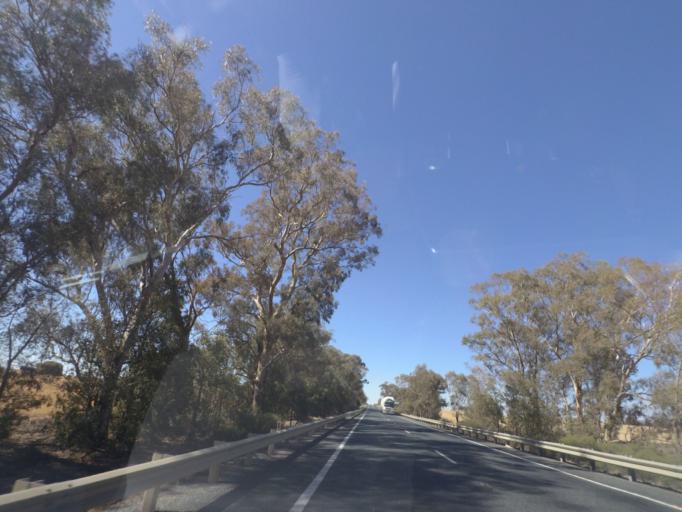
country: AU
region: New South Wales
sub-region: Bland
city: West Wyalong
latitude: -34.1753
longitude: 147.1143
